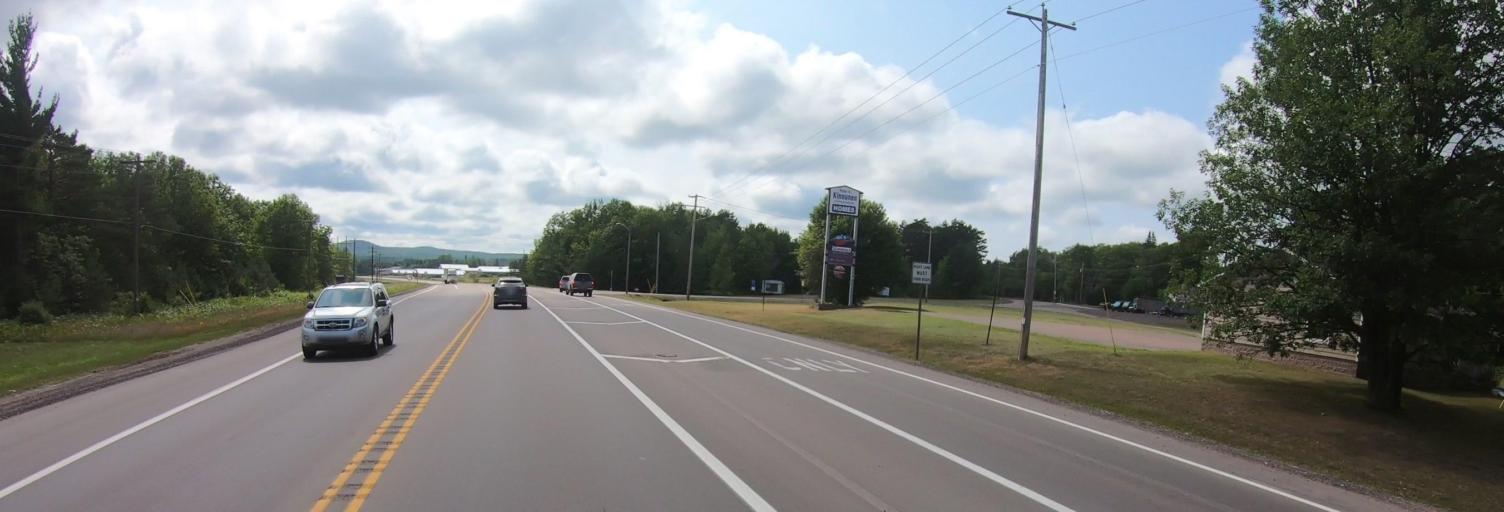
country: US
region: Michigan
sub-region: Houghton County
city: Hancock
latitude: 47.0985
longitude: -88.6146
